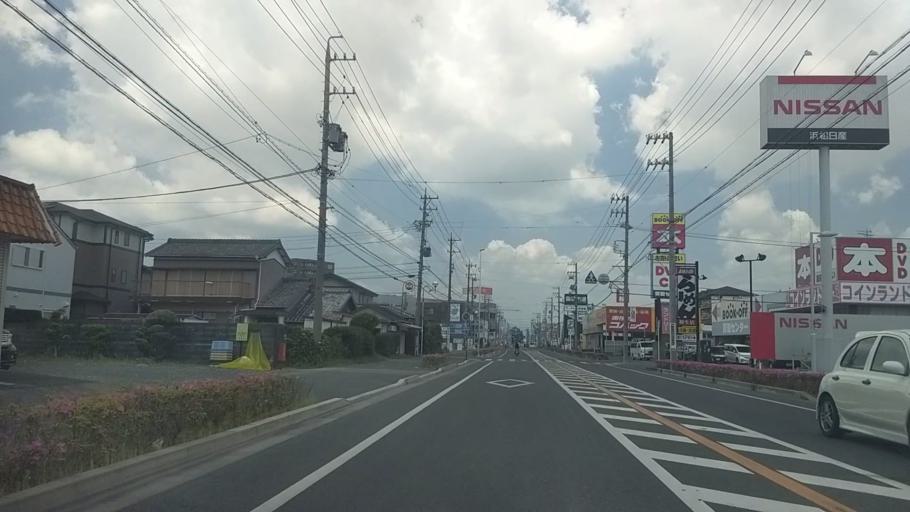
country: JP
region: Shizuoka
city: Hamamatsu
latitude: 34.7605
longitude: 137.7244
